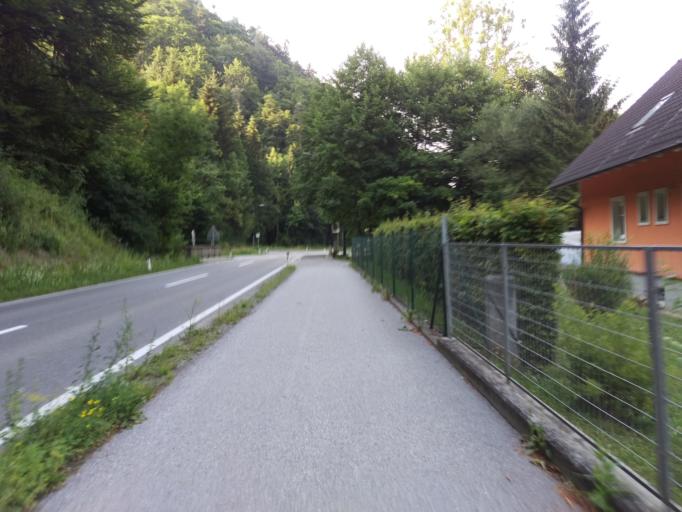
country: AT
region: Styria
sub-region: Politischer Bezirk Graz-Umgebung
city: Thal
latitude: 47.0869
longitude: 15.3717
